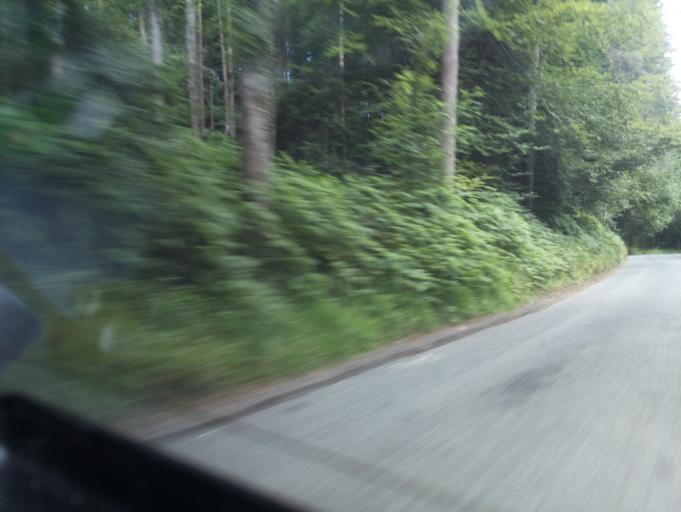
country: GB
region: England
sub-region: Gloucestershire
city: Cinderford
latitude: 51.8032
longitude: -2.4914
